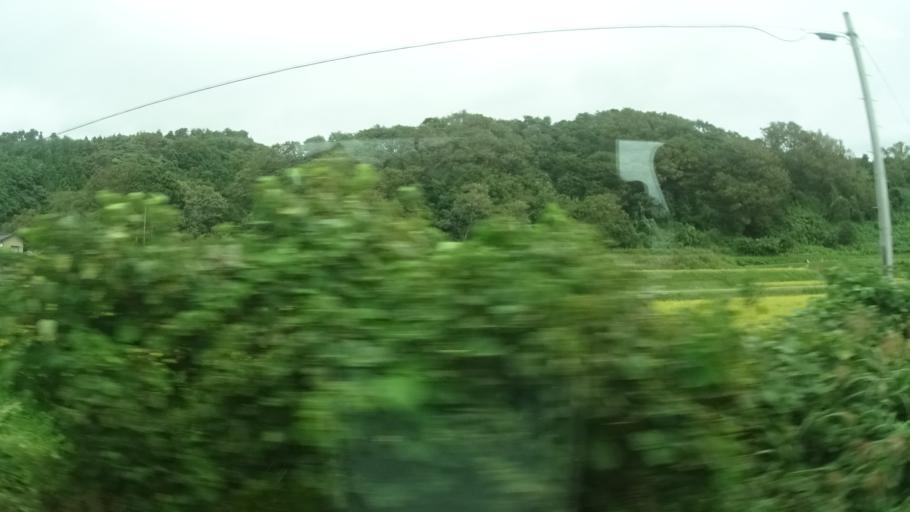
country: JP
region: Niigata
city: Murakami
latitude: 38.3078
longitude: 139.4524
